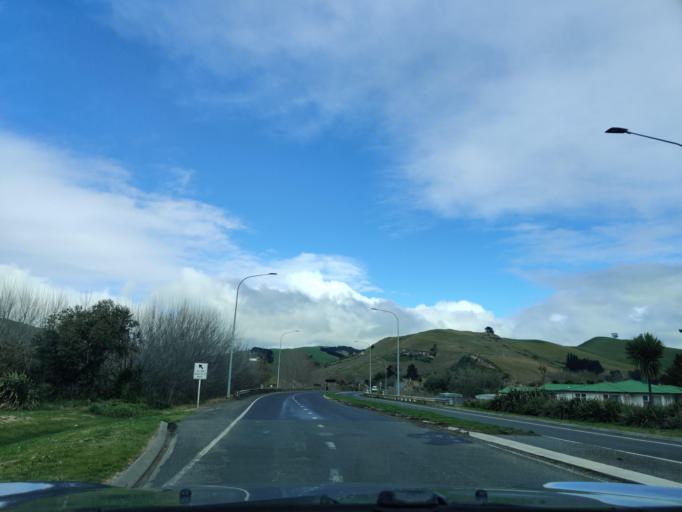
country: NZ
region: Hawke's Bay
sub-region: Hastings District
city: Hastings
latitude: -39.6921
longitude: 176.7937
